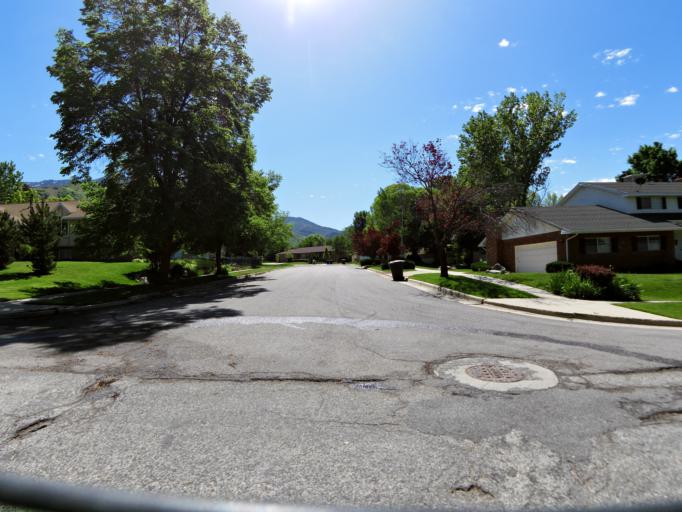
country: US
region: Utah
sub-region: Weber County
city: Uintah
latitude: 41.1692
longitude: -111.9336
